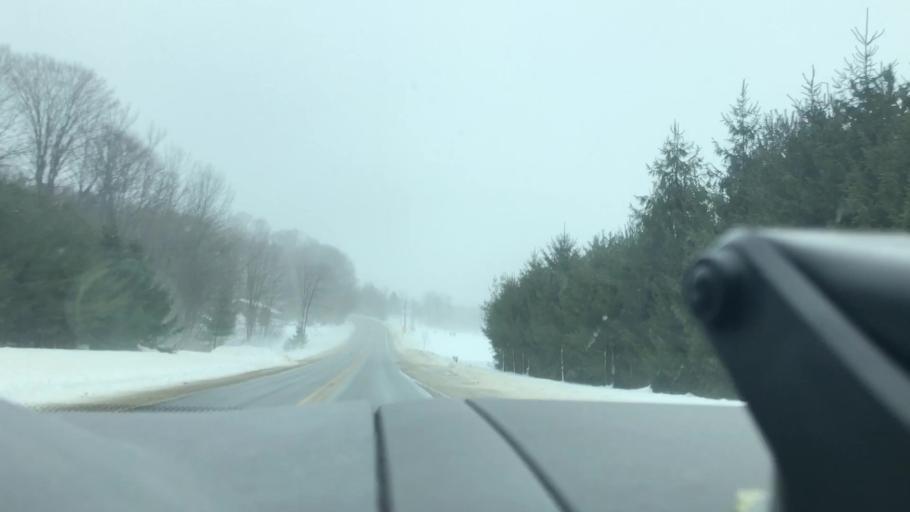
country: US
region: Michigan
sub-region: Charlevoix County
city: East Jordan
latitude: 45.1591
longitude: -85.1640
